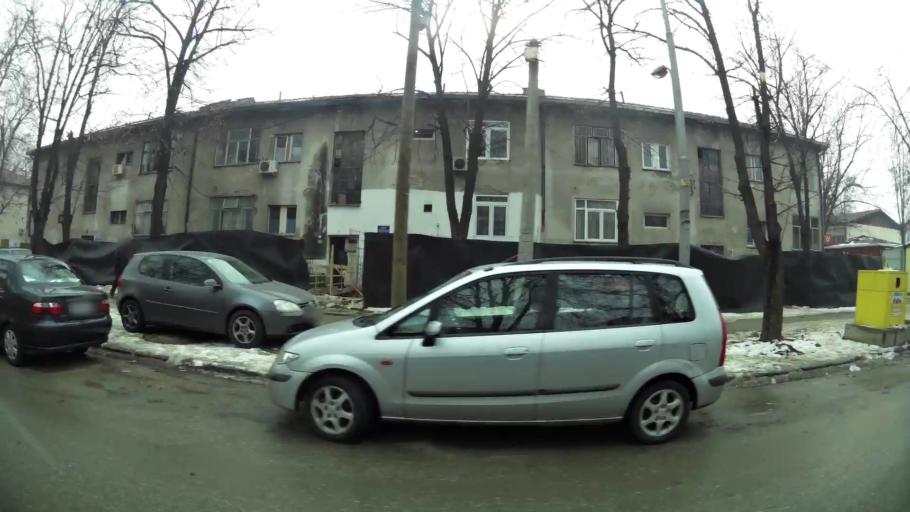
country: MK
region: Cair
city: Cair
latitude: 42.0043
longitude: 21.4664
